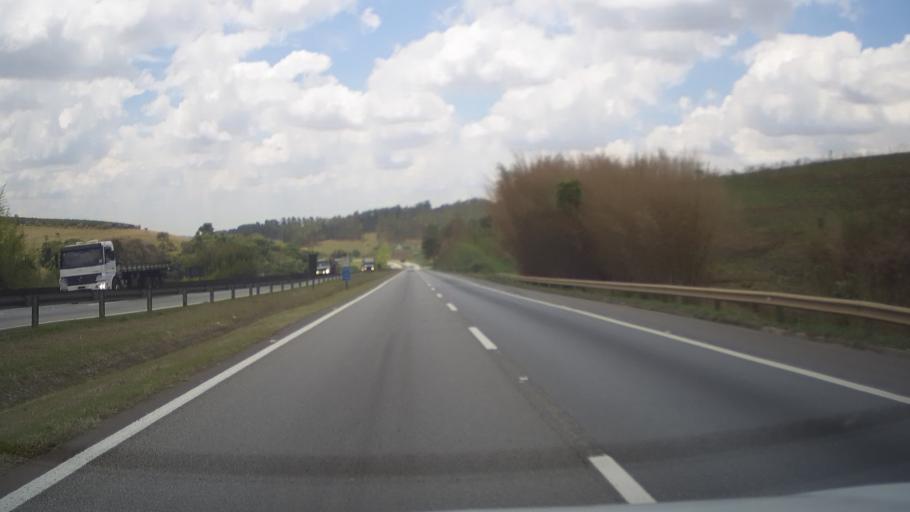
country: BR
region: Minas Gerais
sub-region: Tres Coracoes
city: Tres Coracoes
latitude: -21.6963
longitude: -45.3616
